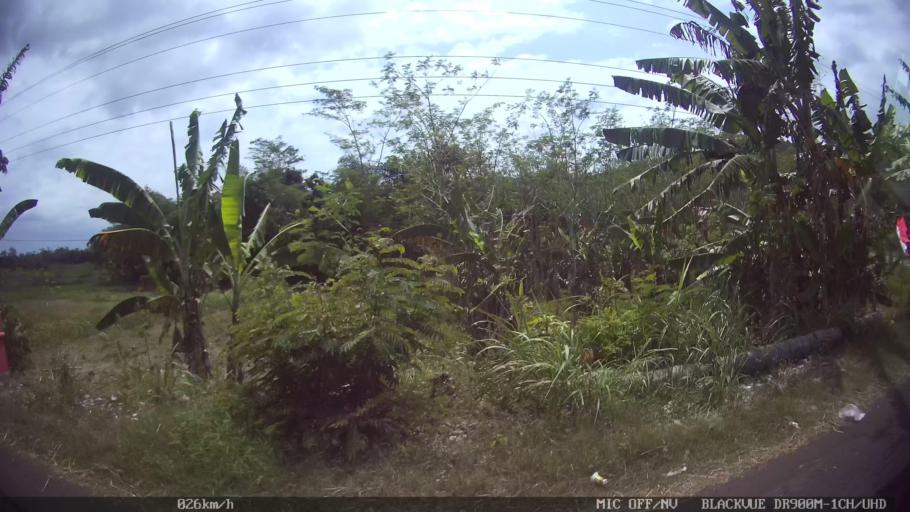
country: ID
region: Central Java
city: Candi Prambanan
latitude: -7.8117
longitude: 110.5105
